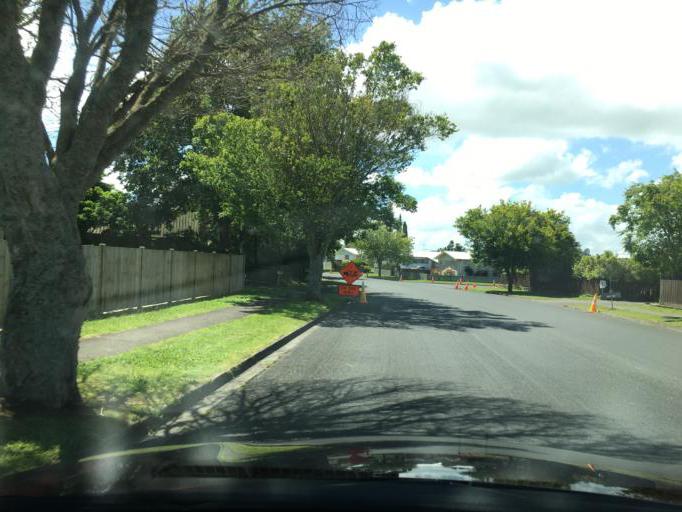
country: NZ
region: Waikato
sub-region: Waipa District
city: Cambridge
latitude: -38.0068
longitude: 175.3363
